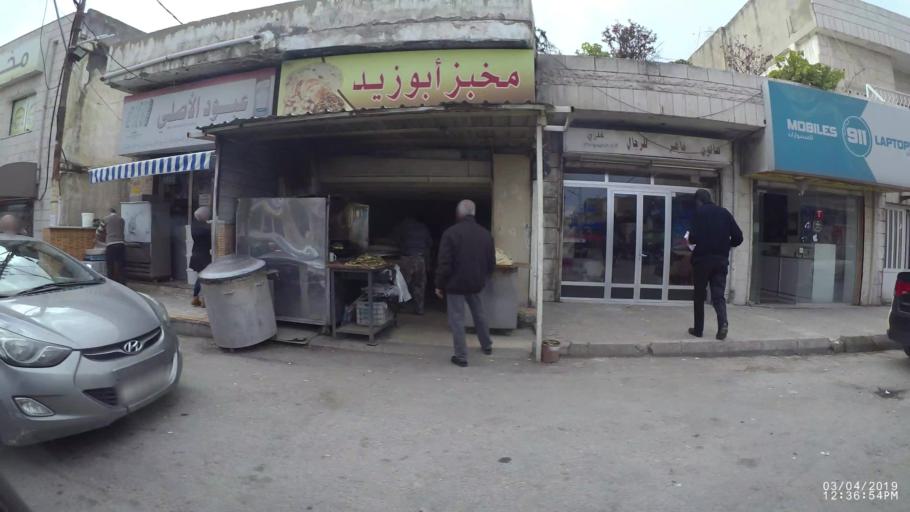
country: JO
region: Amman
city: Wadi as Sir
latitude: 31.9556
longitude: 35.8366
